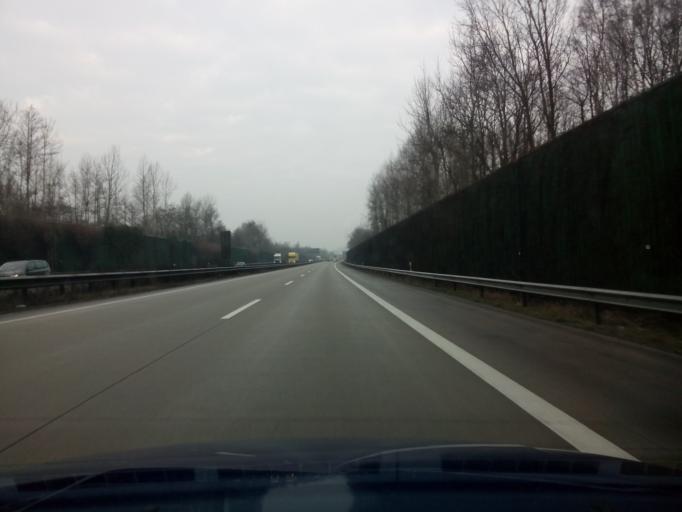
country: DE
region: Lower Saxony
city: Schiffdorf
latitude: 53.5318
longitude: 8.6215
